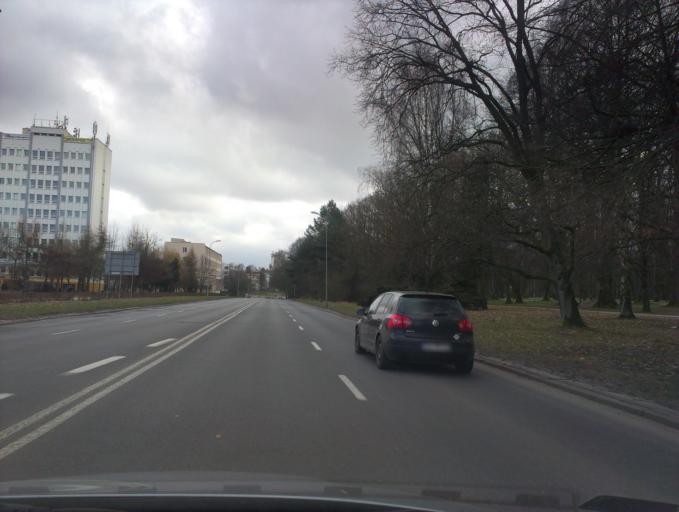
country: PL
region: West Pomeranian Voivodeship
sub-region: Koszalin
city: Koszalin
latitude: 54.1959
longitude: 16.1903
